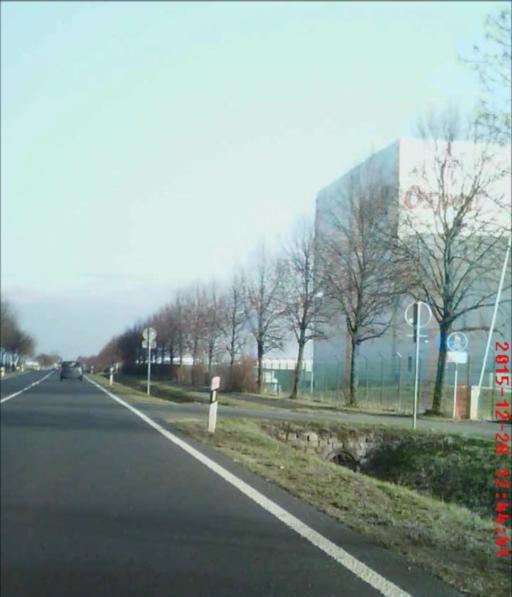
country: DE
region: Thuringia
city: Ossmanstedt
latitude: 51.0073
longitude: 11.4593
